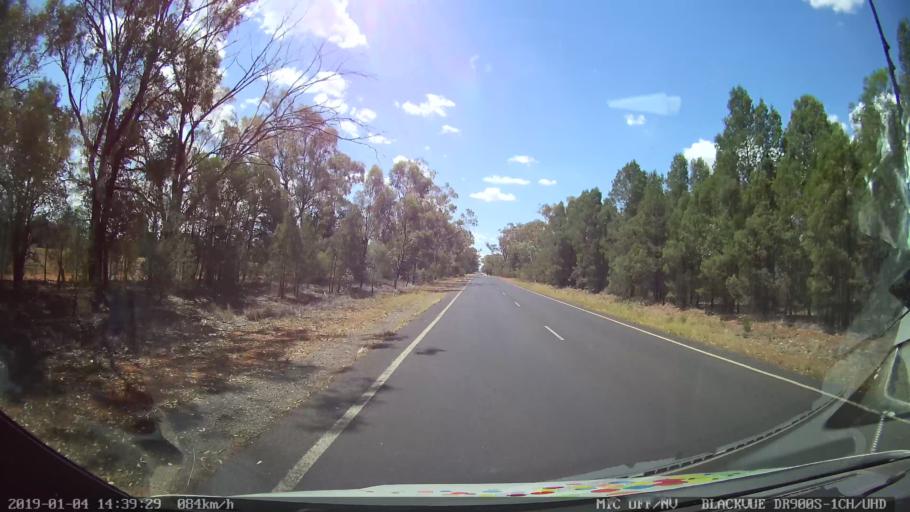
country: AU
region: New South Wales
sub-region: Dubbo Municipality
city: Dubbo
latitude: -32.1642
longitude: 148.6330
